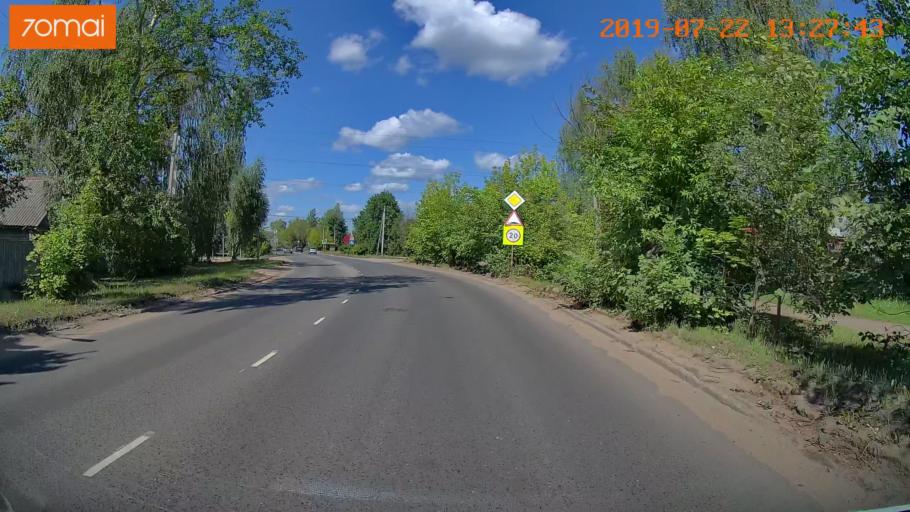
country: RU
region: Ivanovo
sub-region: Gorod Ivanovo
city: Ivanovo
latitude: 57.0375
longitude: 40.9507
